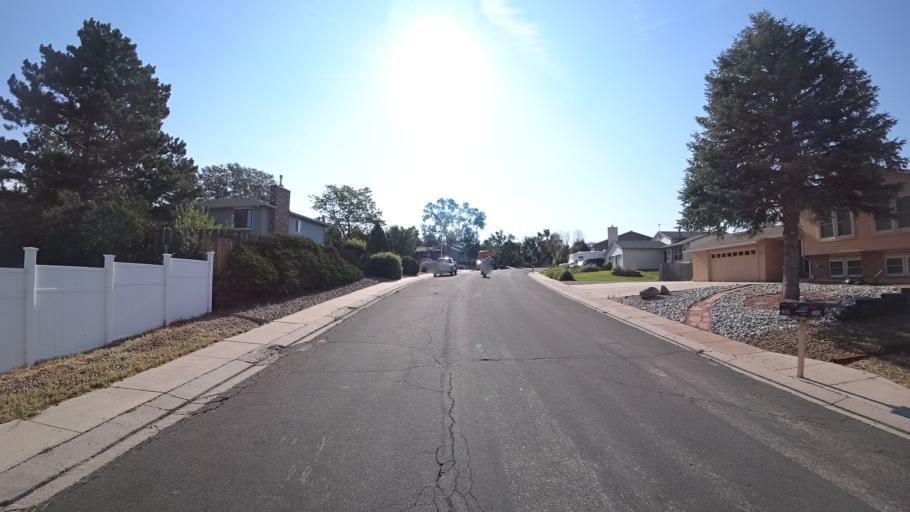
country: US
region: Colorado
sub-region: El Paso County
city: Air Force Academy
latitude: 38.9448
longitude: -104.7833
